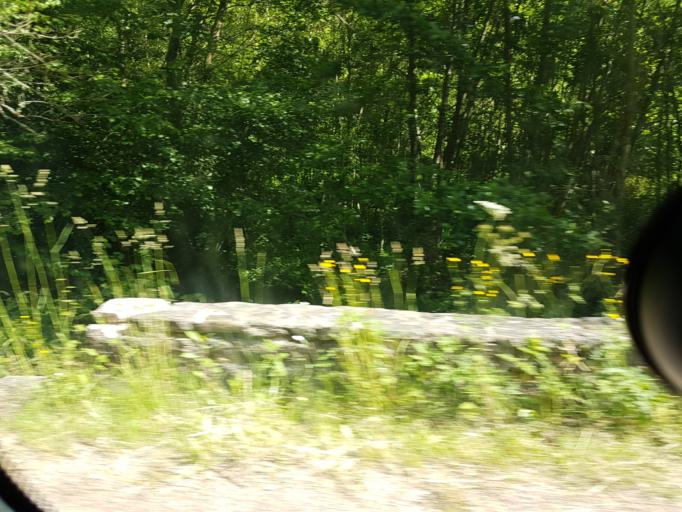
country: FR
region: Bourgogne
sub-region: Departement de la Cote-d'Or
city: Saulieu
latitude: 47.1645
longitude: 4.1665
